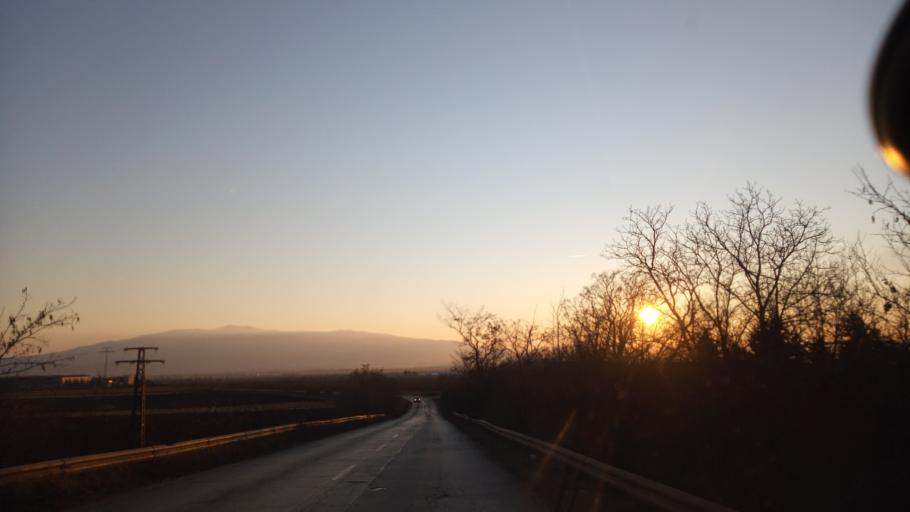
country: BG
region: Sofia-Capital
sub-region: Stolichna Obshtina
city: Bukhovo
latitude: 42.7689
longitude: 23.4949
